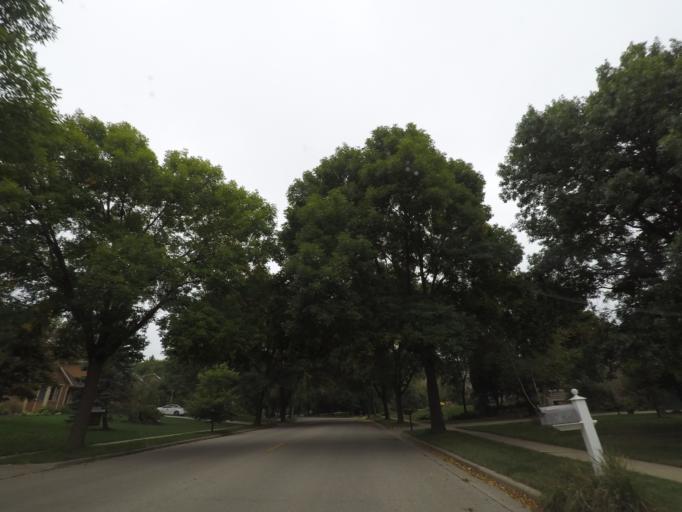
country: US
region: Wisconsin
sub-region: Dane County
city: Middleton
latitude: 43.0845
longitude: -89.5111
